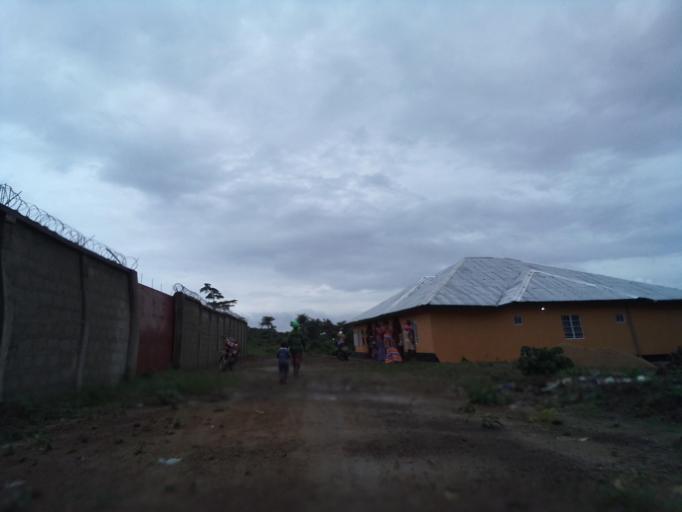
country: SL
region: Eastern Province
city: Kenema
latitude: 7.8763
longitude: -11.1559
